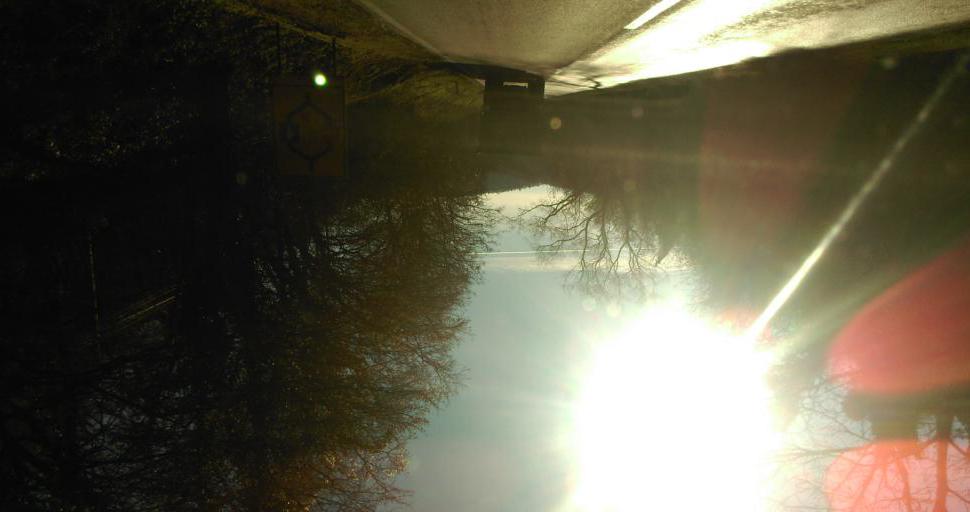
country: RS
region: Autonomna Pokrajina Vojvodina
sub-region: Juznobacki Okrug
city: Novi Sad
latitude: 45.1840
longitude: 19.8396
